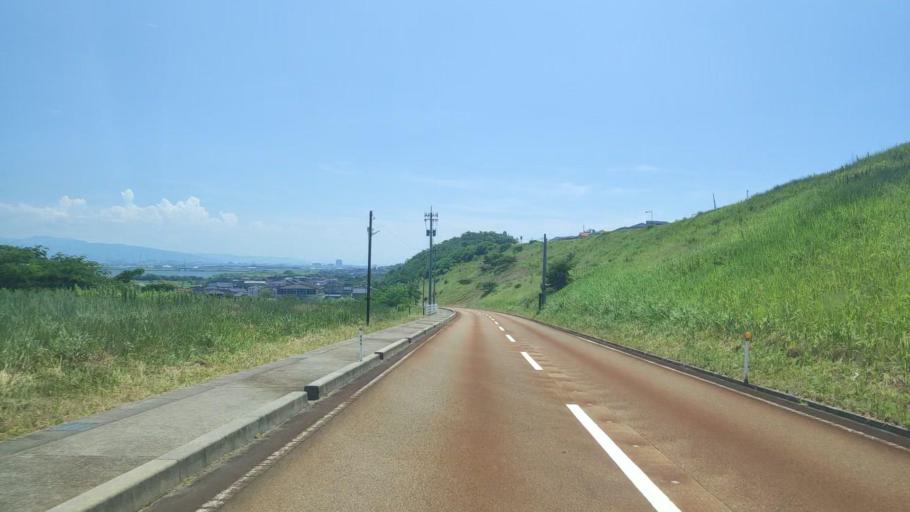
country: JP
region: Ishikawa
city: Tsubata
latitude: 36.6700
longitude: 136.6586
